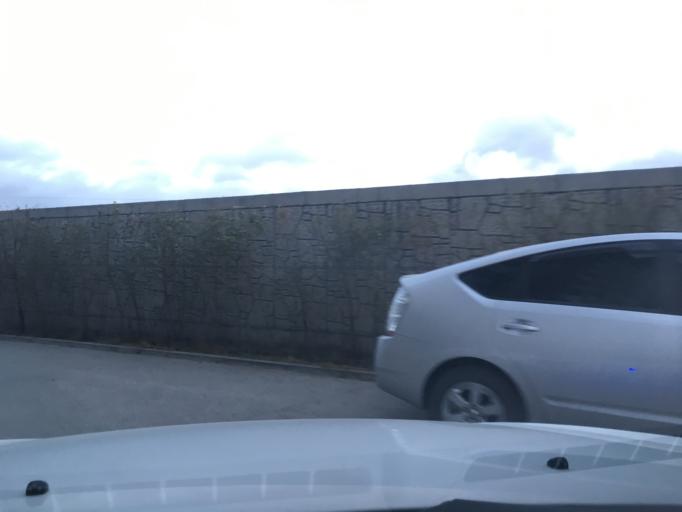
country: MN
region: Ulaanbaatar
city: Ulaanbaatar
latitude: 47.9120
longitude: 106.8640
